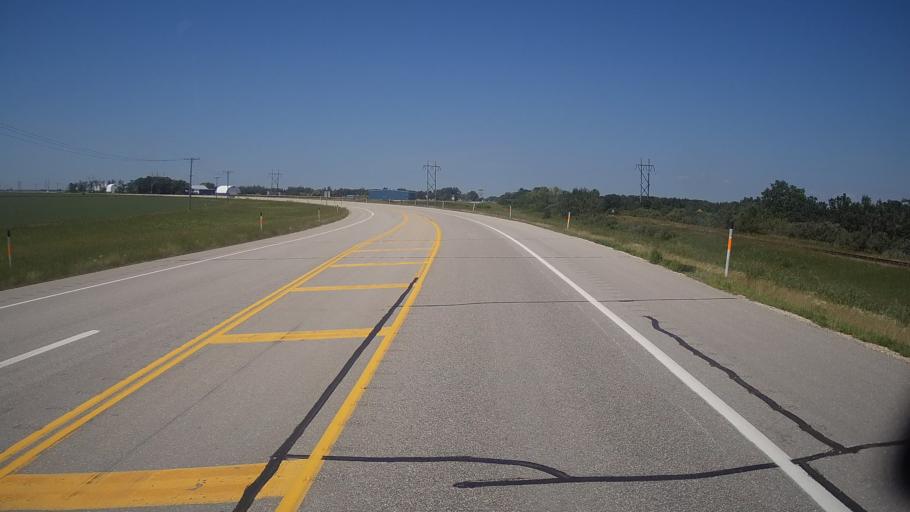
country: CA
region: Manitoba
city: Stonewall
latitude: 50.1213
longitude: -97.5299
